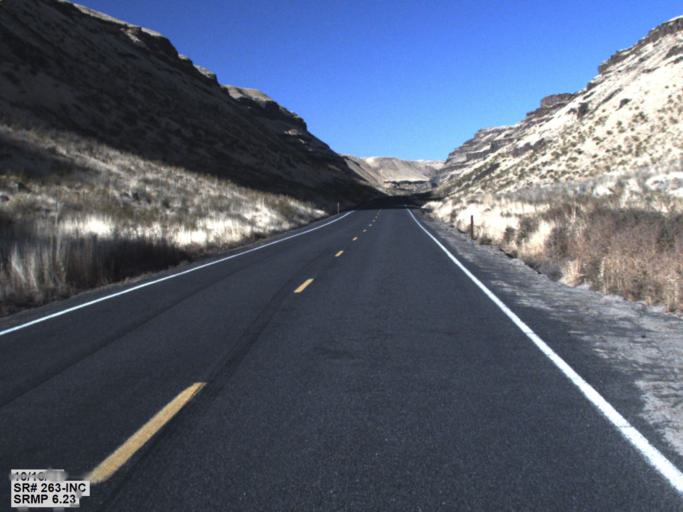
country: US
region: Washington
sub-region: Franklin County
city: Connell
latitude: 46.6042
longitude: -118.5513
